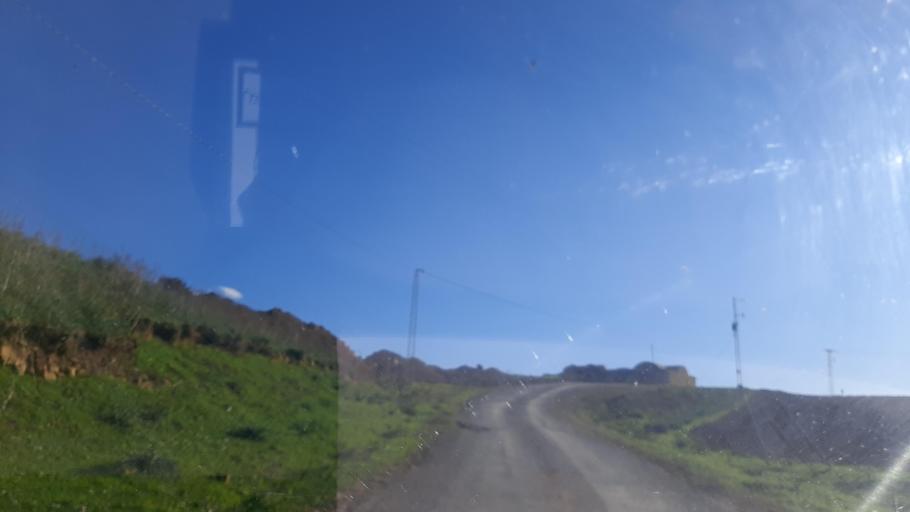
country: TN
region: Nabul
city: El Mida
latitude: 36.8084
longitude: 10.8457
